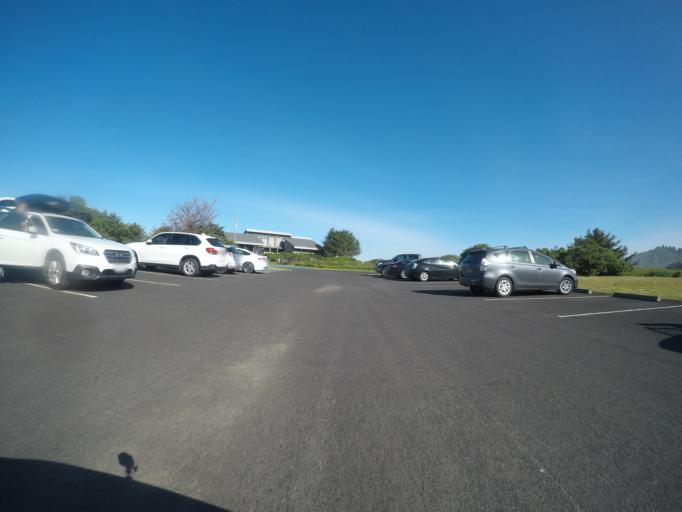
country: US
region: California
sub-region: Humboldt County
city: Westhaven-Moonstone
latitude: 41.2864
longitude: -124.0900
